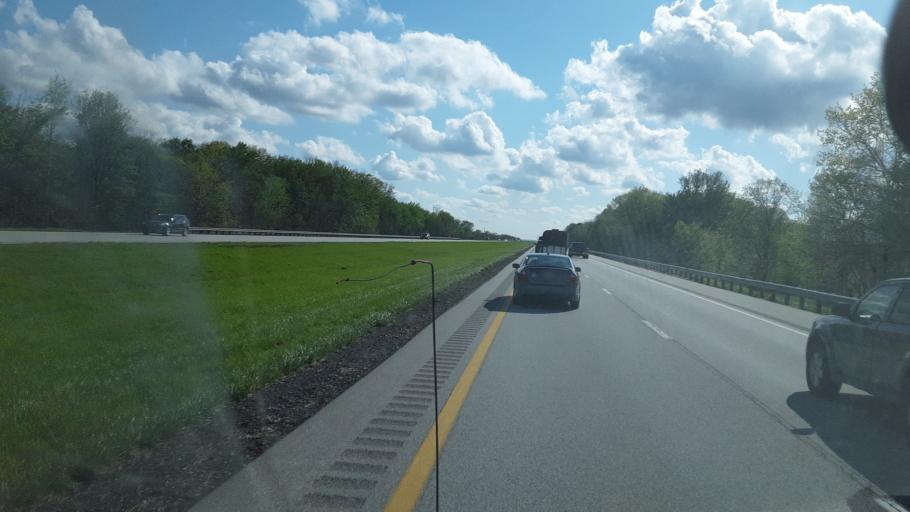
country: US
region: Ohio
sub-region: Ashtabula County
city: Ashtabula
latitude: 41.8036
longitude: -80.8272
